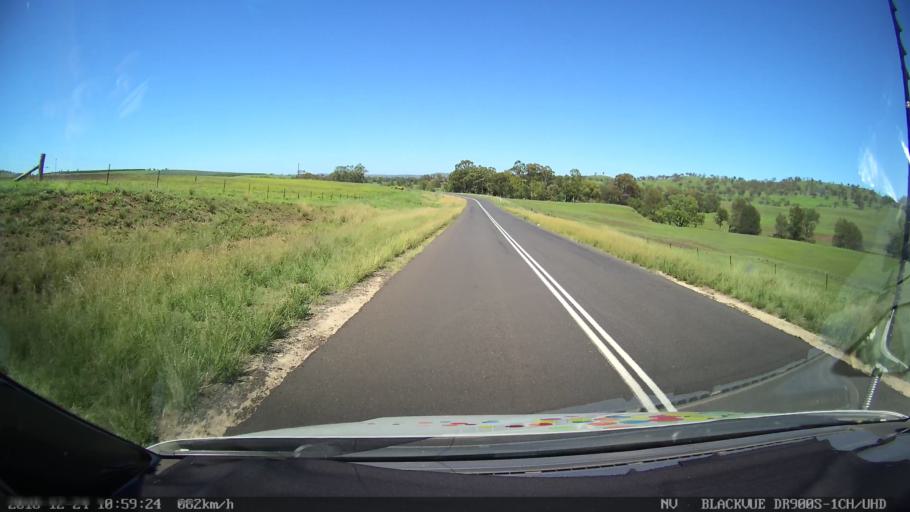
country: AU
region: New South Wales
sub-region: Upper Hunter Shire
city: Merriwa
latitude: -32.0642
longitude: 150.3937
